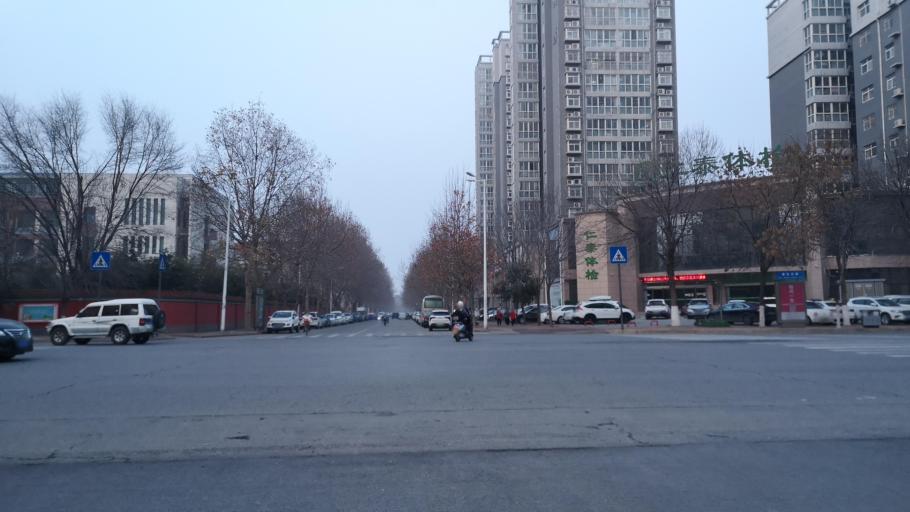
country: CN
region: Henan Sheng
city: Zhongyuanlu
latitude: 35.7531
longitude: 115.0606
